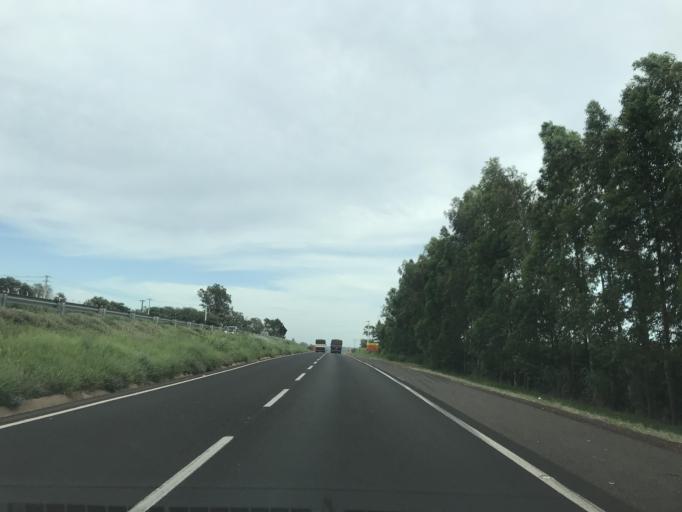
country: BR
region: Parana
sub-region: Alto Parana
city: Alto Parana
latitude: -23.1225
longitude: -52.3101
